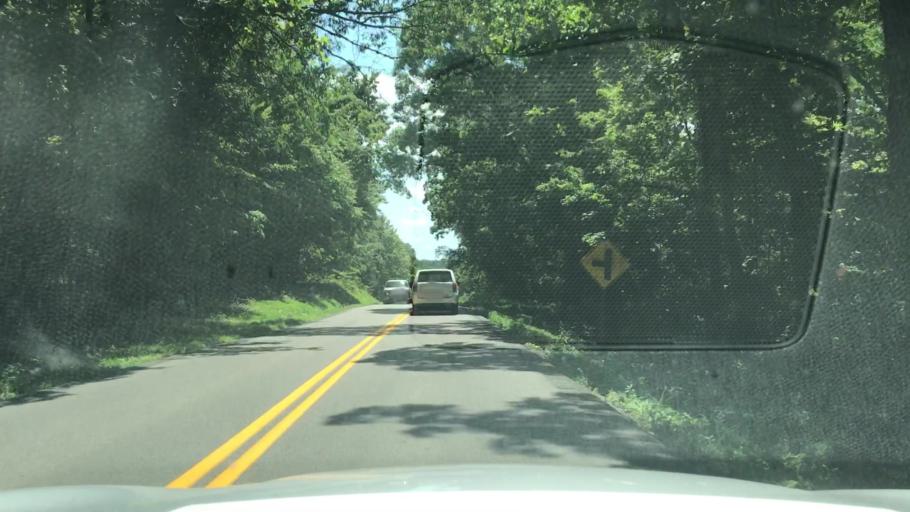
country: US
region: Kentucky
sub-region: Christian County
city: Hopkinsville
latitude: 36.8954
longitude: -87.4517
